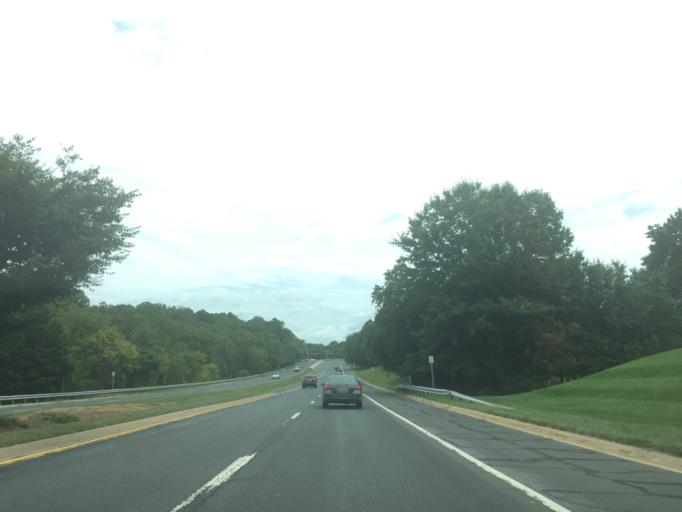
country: US
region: Maryland
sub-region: Montgomery County
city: Gaithersburg
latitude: 39.1591
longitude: -77.1979
